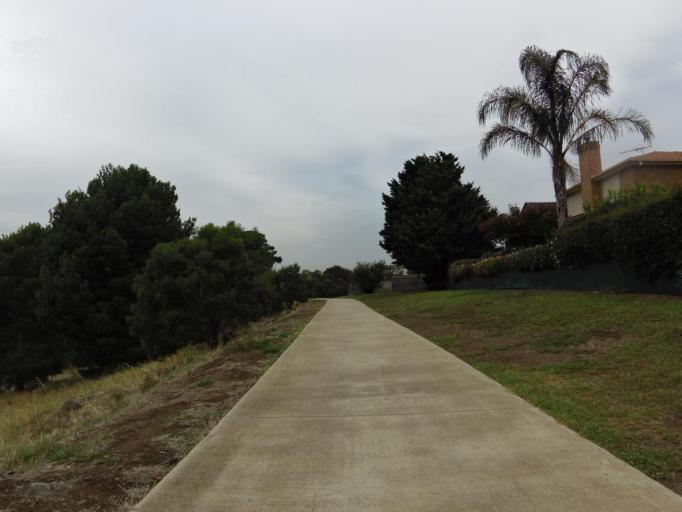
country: AU
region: Victoria
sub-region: Brimbank
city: Keilor Downs
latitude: -37.7113
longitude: 144.8170
